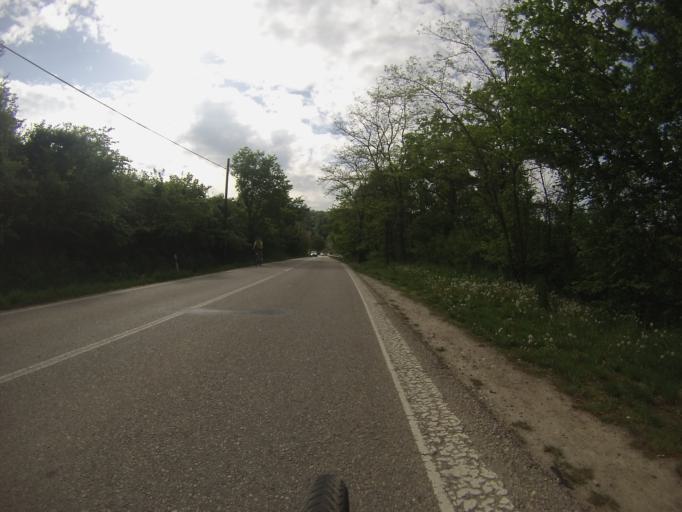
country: CZ
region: South Moravian
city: Troubsko
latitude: 49.2340
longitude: 16.5080
